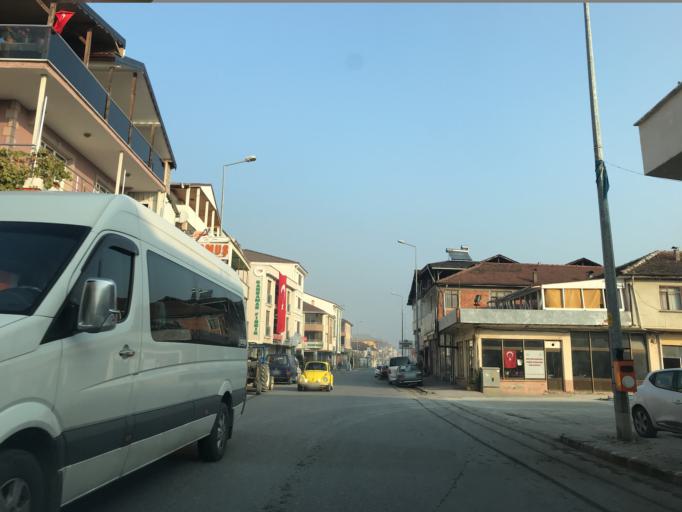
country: TR
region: Duzce
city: Cumayeri
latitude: 40.8766
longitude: 30.9502
